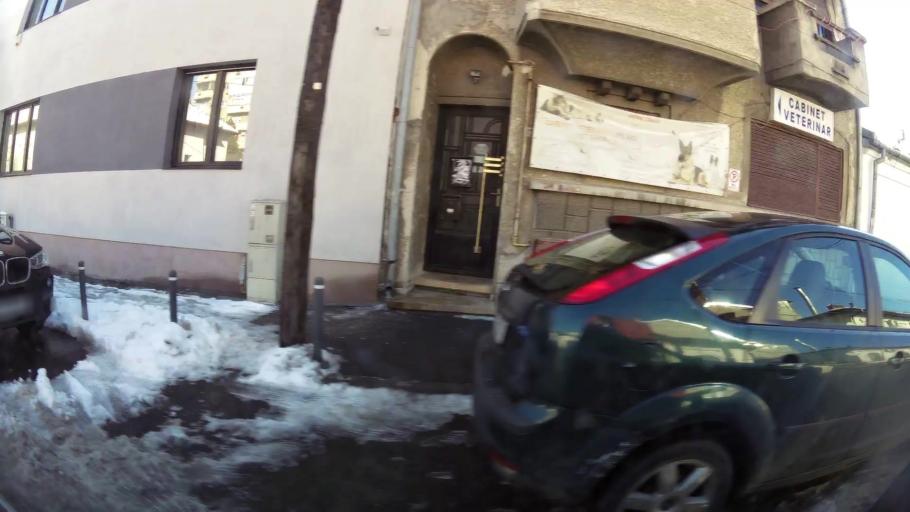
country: RO
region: Bucuresti
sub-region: Municipiul Bucuresti
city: Bucuresti
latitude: 44.4234
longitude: 26.0777
